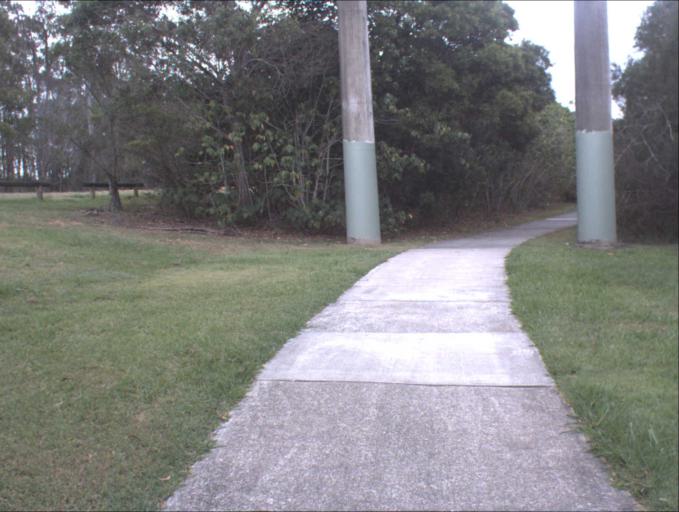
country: AU
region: Queensland
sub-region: Logan
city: Slacks Creek
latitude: -27.6443
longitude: 153.1359
